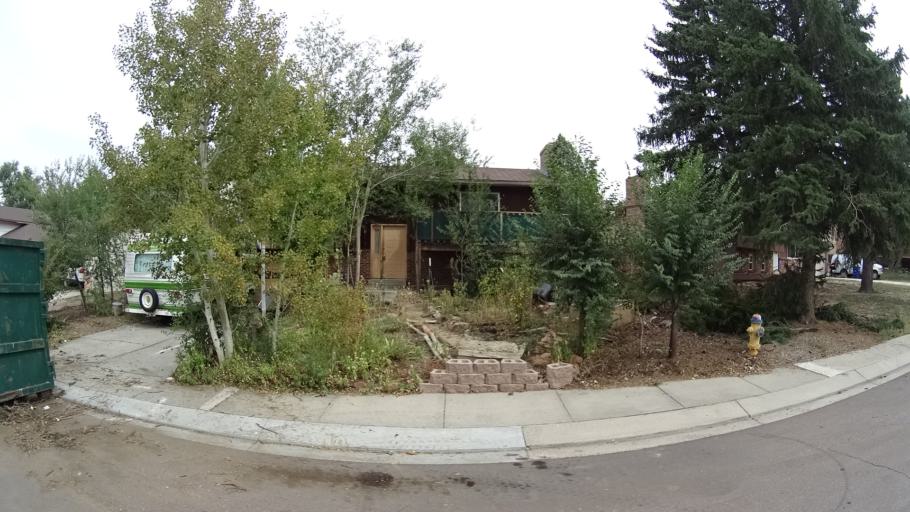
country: US
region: Colorado
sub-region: El Paso County
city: Cimarron Hills
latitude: 38.8909
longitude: -104.7330
